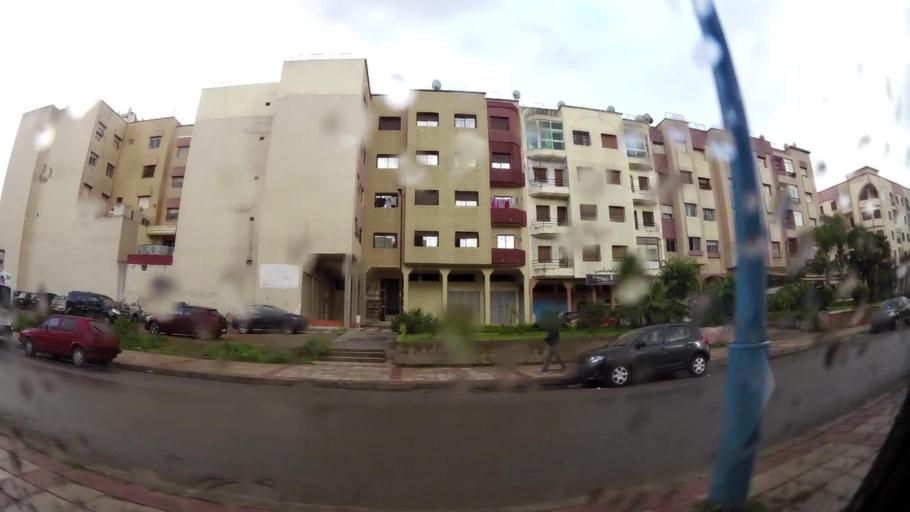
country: MA
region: Grand Casablanca
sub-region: Mohammedia
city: Mohammedia
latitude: 33.6790
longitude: -7.3862
